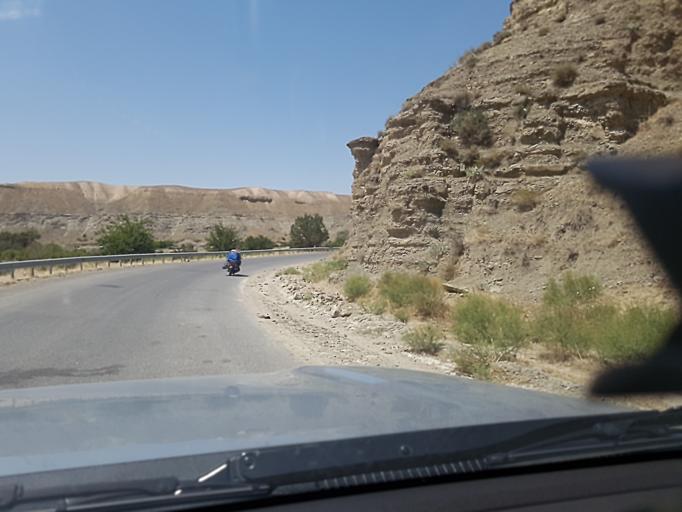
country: TM
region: Balkan
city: Magtymguly
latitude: 38.4479
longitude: 56.5198
